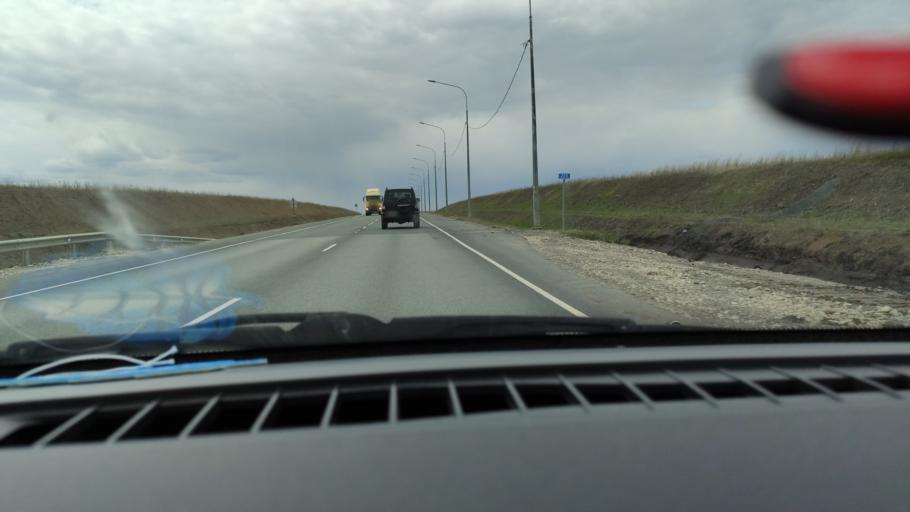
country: RU
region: Saratov
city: Yelshanka
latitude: 51.8307
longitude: 46.4351
